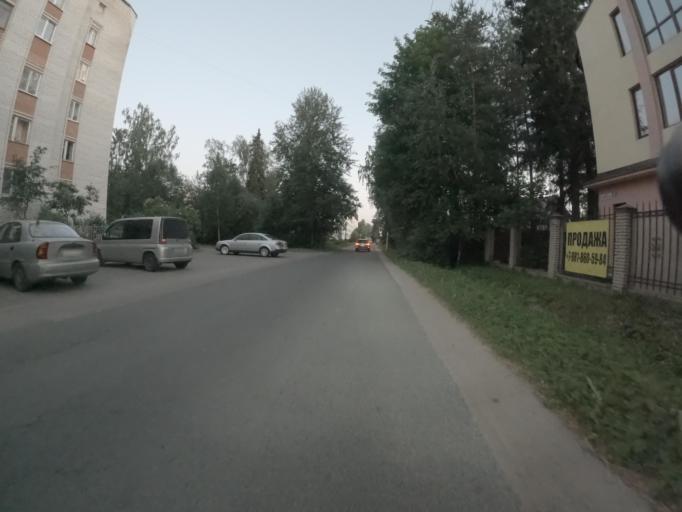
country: RU
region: Leningrad
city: Vsevolozhsk
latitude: 60.0139
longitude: 30.6140
